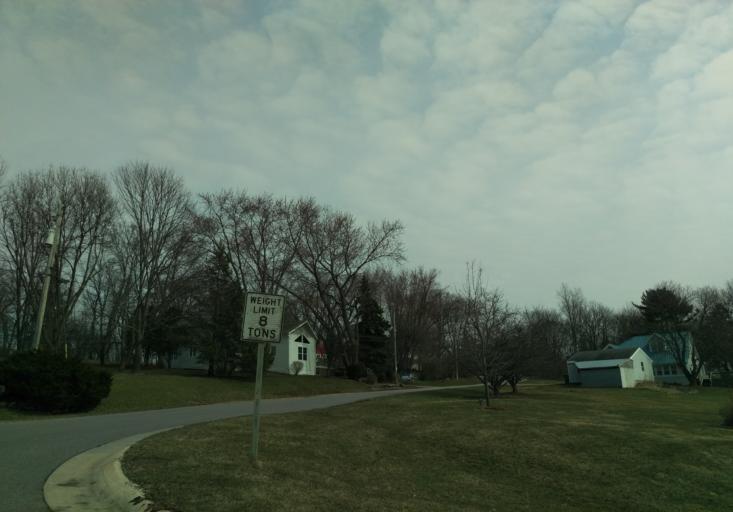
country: US
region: Wisconsin
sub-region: Columbia County
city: Lodi
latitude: 43.3074
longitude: -89.5351
